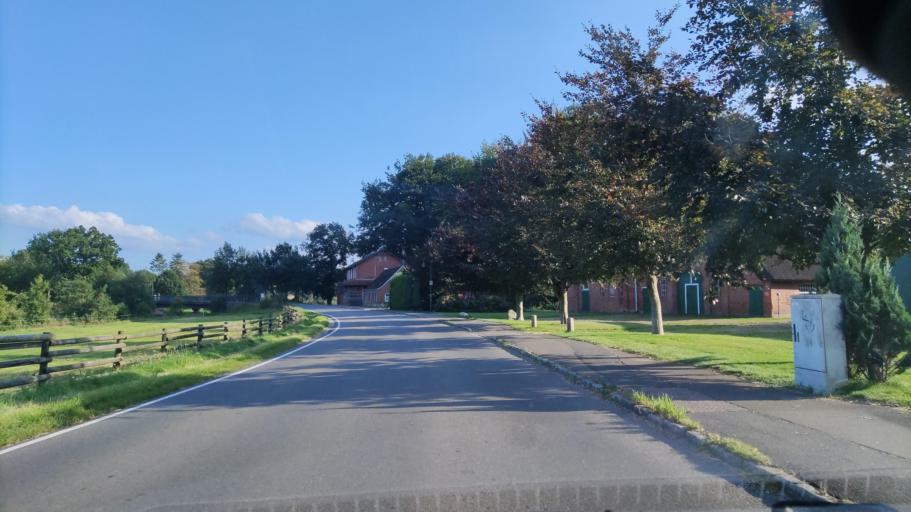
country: DE
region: Schleswig-Holstein
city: Willenscharen
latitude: 54.0113
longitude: 9.8048
